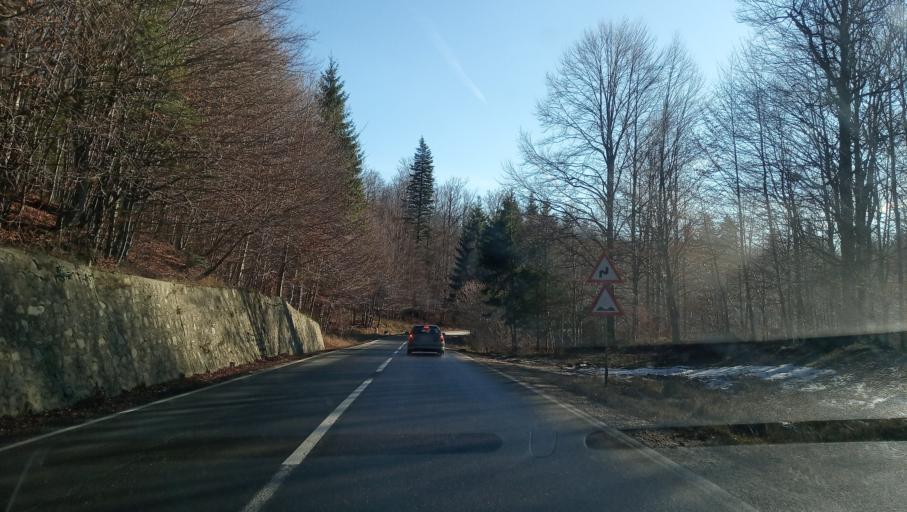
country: RO
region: Brasov
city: Crivina
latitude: 45.4669
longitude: 25.9390
